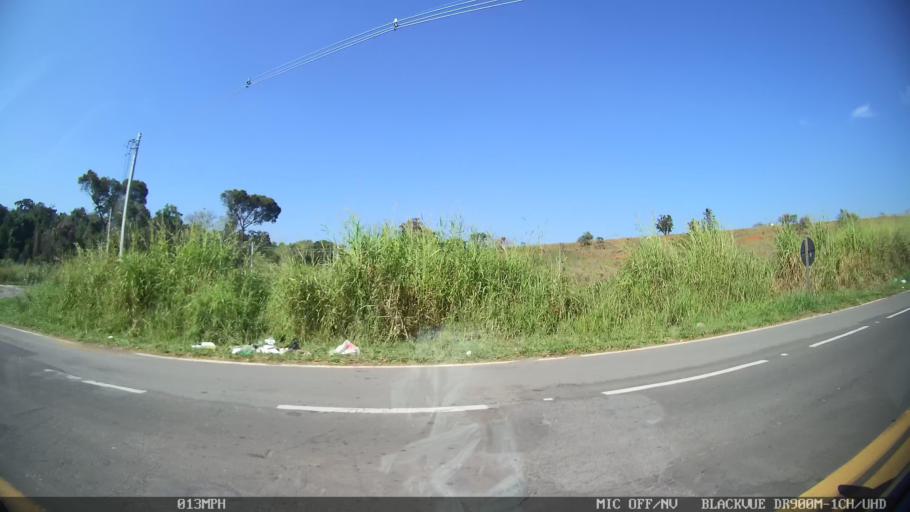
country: BR
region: Sao Paulo
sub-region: Valinhos
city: Valinhos
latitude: -23.0129
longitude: -47.0931
